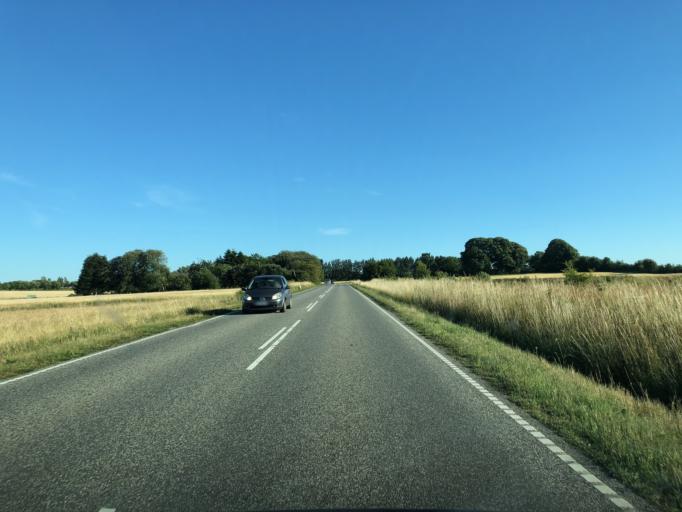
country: DK
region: Central Jutland
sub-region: Skanderborg Kommune
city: Stilling
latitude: 56.0855
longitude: 9.9715
